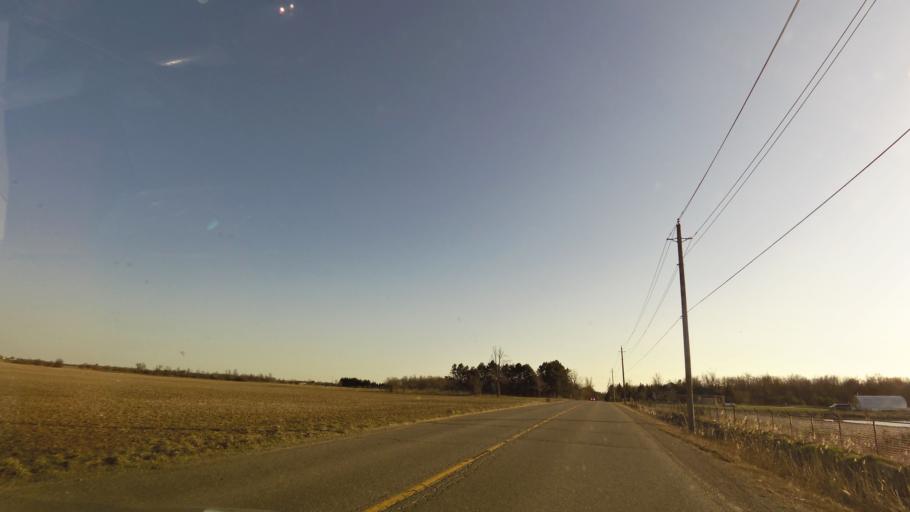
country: CA
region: Ontario
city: Brampton
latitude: 43.8556
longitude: -79.7368
